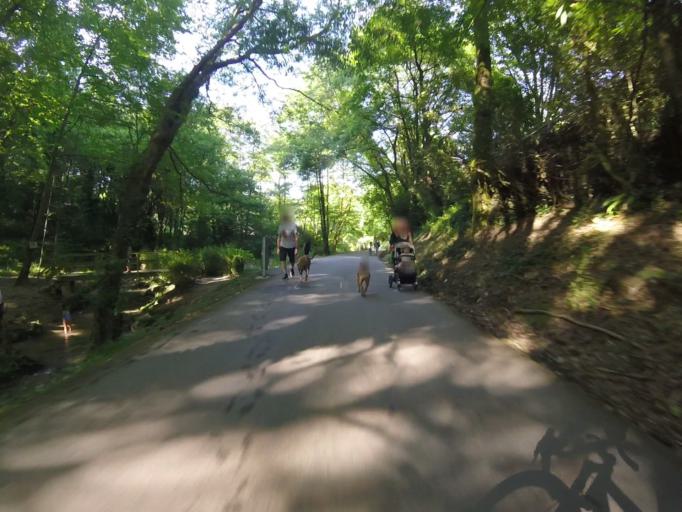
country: ES
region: Basque Country
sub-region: Provincia de Guipuzcoa
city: Pasaia
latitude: 43.3105
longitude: -1.9242
